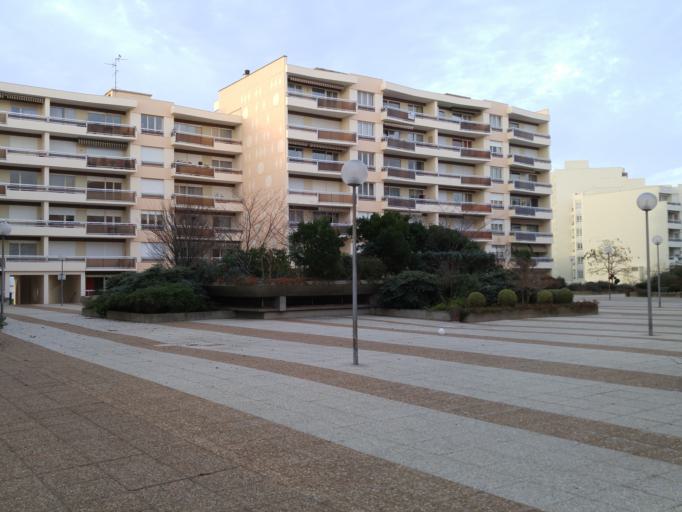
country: FR
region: Pays de la Loire
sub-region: Departement de Maine-et-Loire
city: Angers
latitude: 47.4538
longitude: -0.5554
